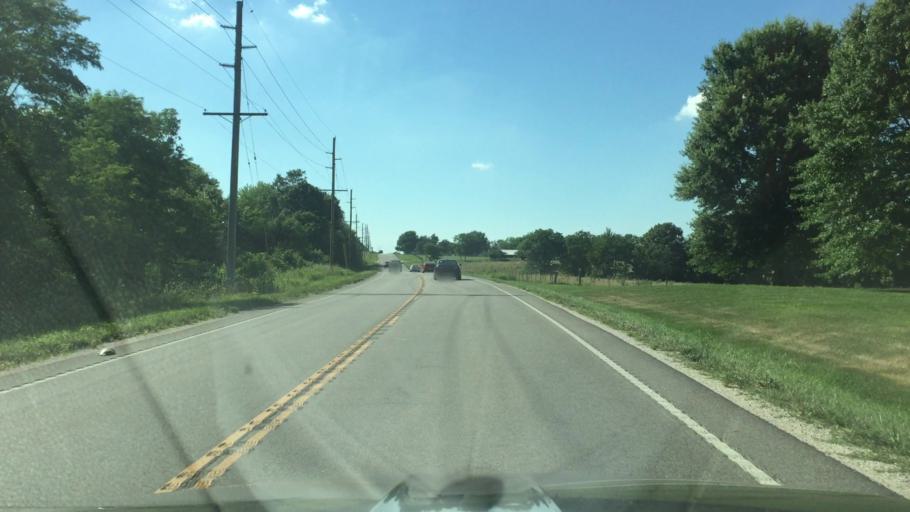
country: US
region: Missouri
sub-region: Morgan County
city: Versailles
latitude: 38.4420
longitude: -92.7882
